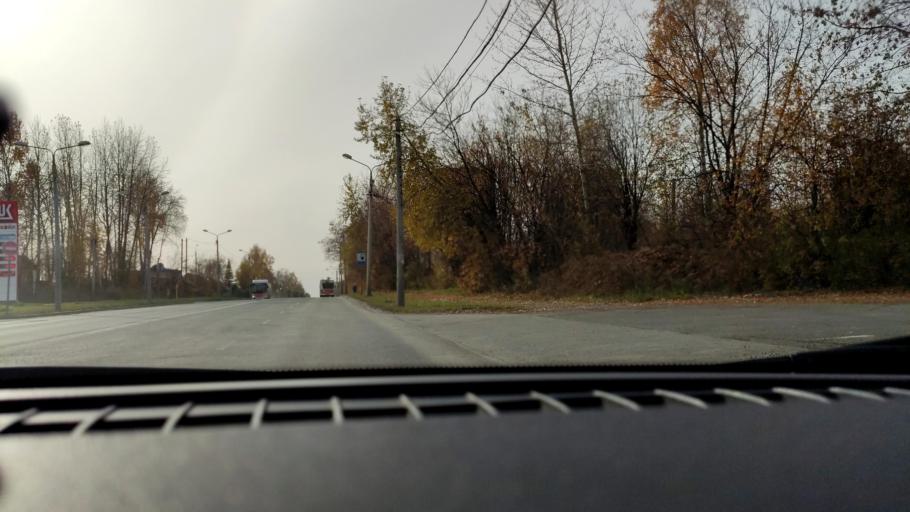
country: RU
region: Perm
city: Perm
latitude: 58.0656
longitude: 56.3649
